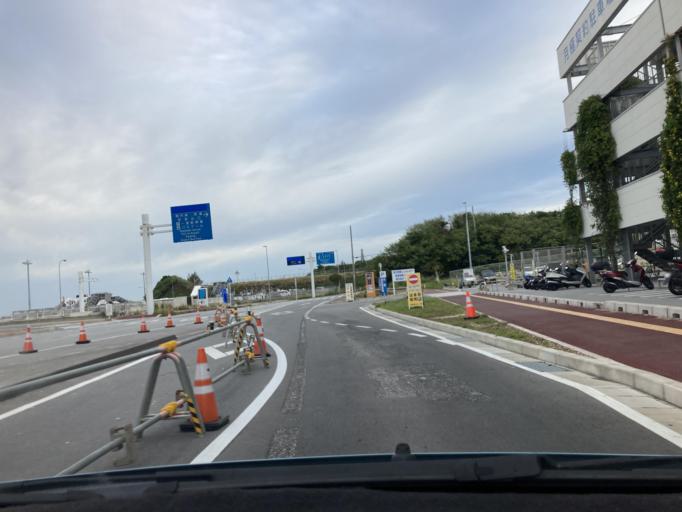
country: JP
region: Okinawa
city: Naha-shi
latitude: 26.2114
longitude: 127.6511
